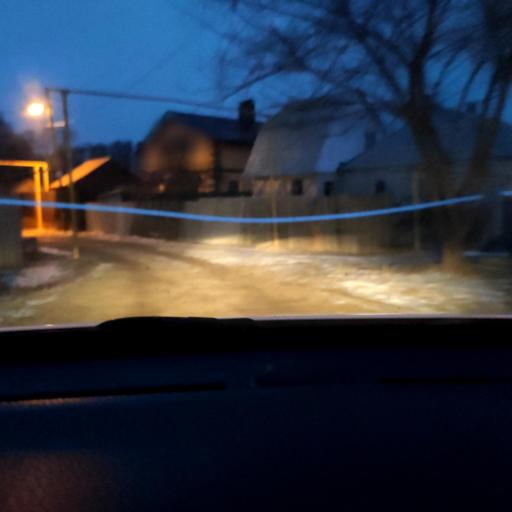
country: RU
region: Voronezj
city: Somovo
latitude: 51.7419
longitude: 39.3563
